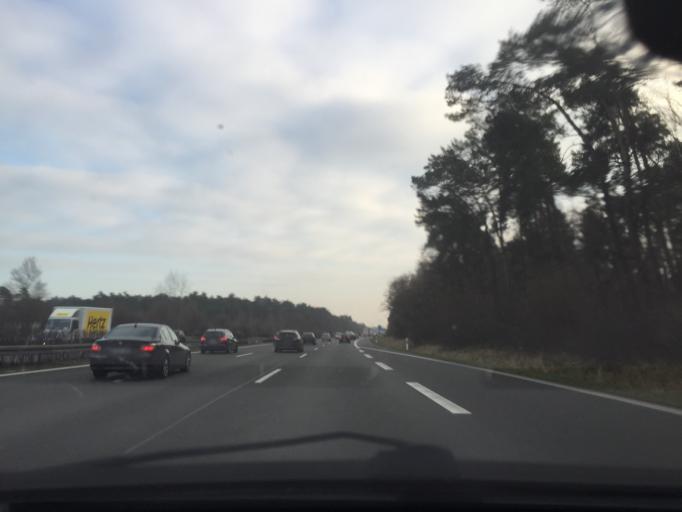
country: DE
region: Brandenburg
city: Fichtenwalde
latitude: 52.3192
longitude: 12.8576
